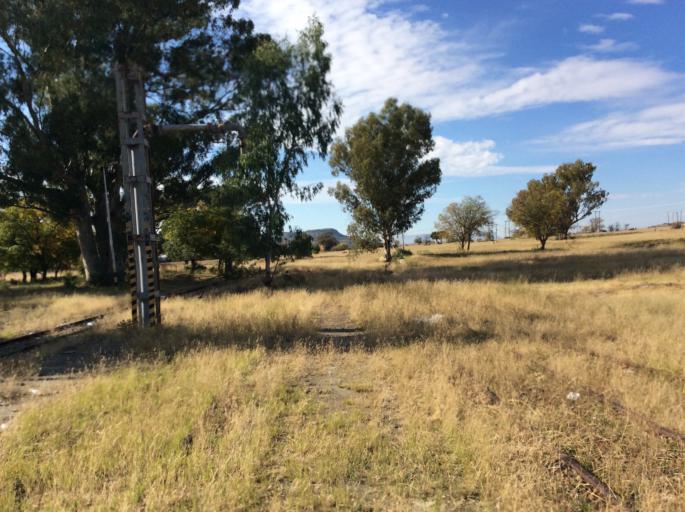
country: LS
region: Mafeteng
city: Mafeteng
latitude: -29.7321
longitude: 27.0281
